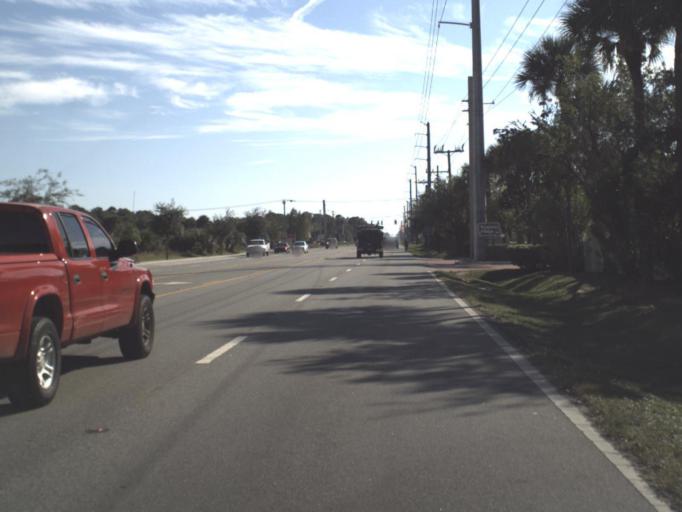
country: US
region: Florida
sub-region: Brevard County
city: June Park
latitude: 28.1158
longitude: -80.6727
